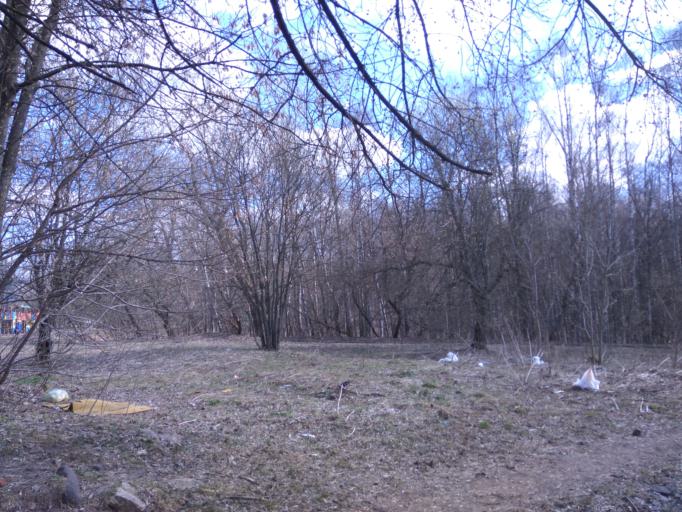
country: RU
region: Moskovskaya
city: Izmaylovo
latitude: 55.7881
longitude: 37.7973
